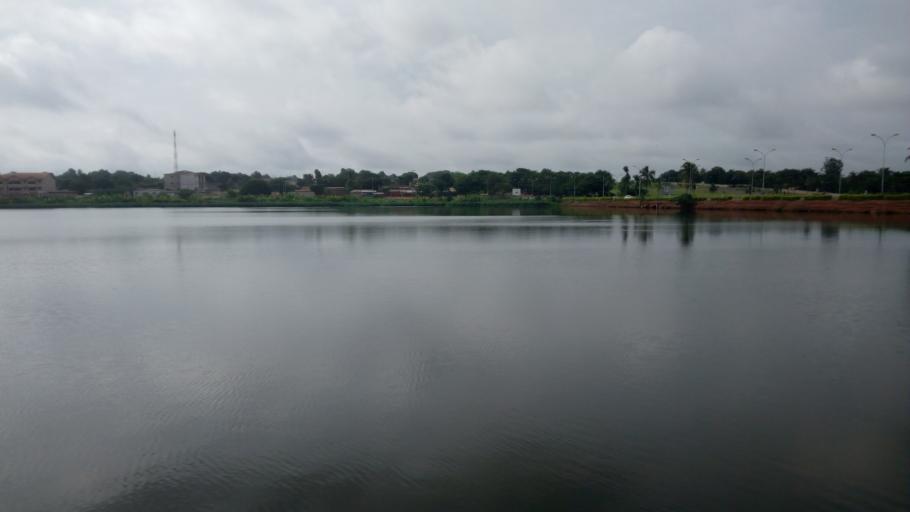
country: CI
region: Lacs
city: Yamoussoukro
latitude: 6.8225
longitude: -5.2706
